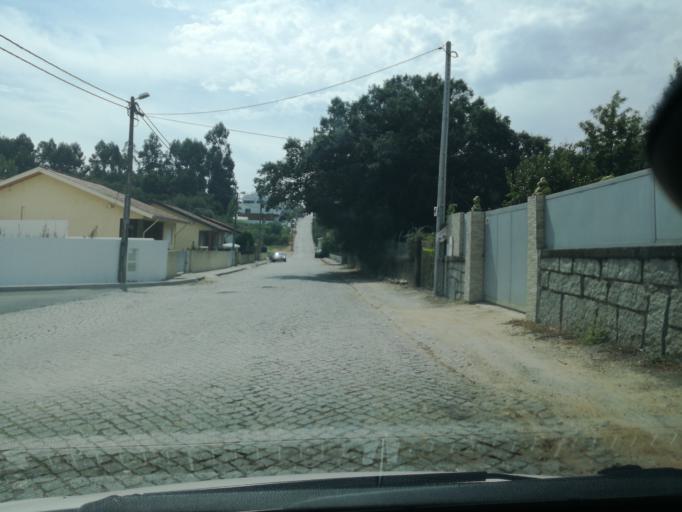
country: PT
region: Porto
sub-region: Vila Nova de Gaia
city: Grijo
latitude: 41.0214
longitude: -8.5863
